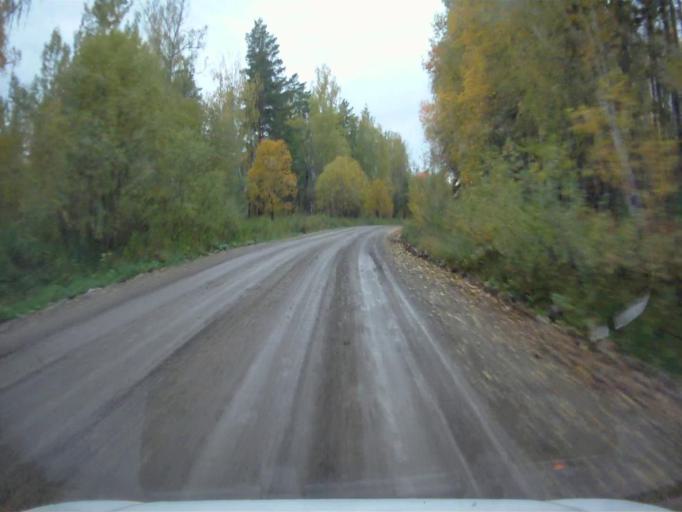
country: RU
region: Chelyabinsk
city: Nyazepetrovsk
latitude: 56.1114
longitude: 59.3712
